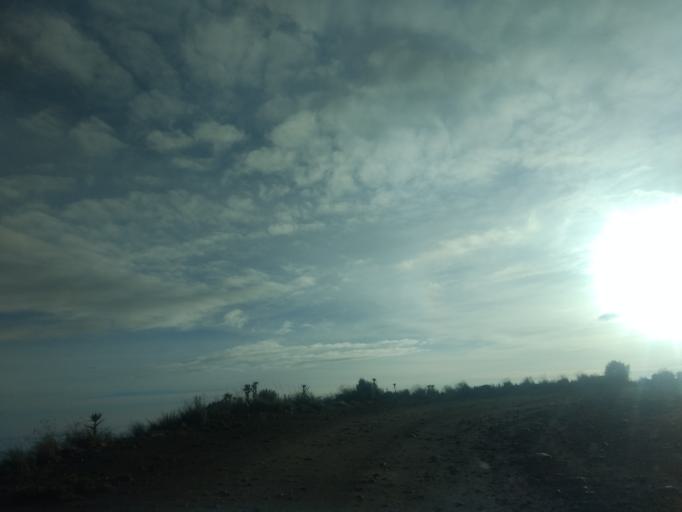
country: MX
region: Mexico
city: Cerro La Calera
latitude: 19.1213
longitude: -99.7558
